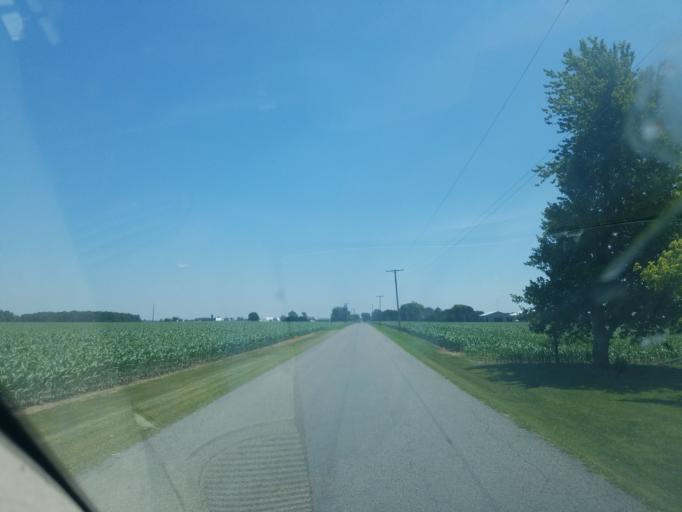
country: US
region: Ohio
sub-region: Allen County
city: Spencerville
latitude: 40.7575
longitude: -84.3809
